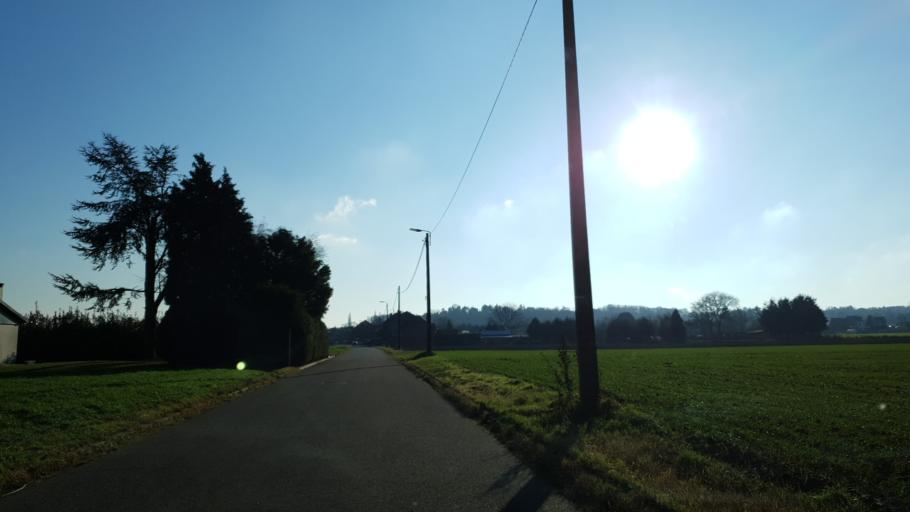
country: BE
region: Flanders
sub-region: Provincie Vlaams-Brabant
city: Herent
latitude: 50.9095
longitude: 4.6936
